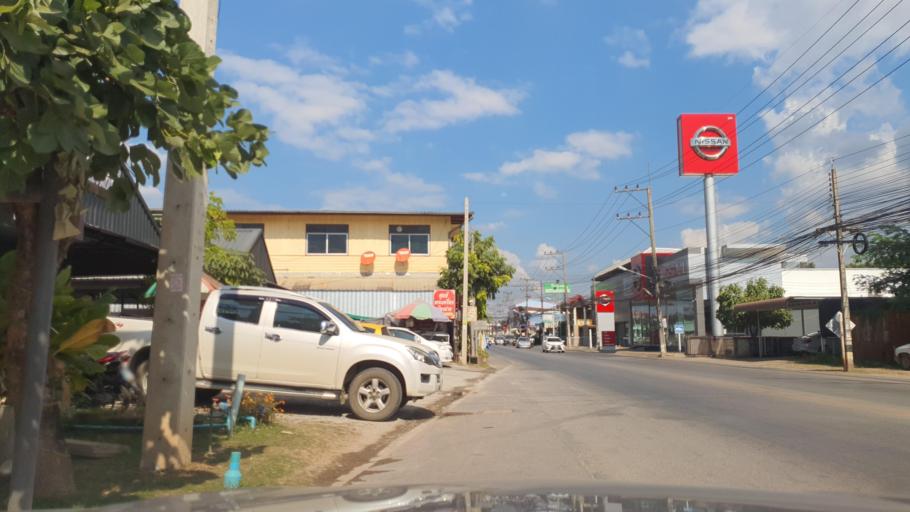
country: TH
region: Nan
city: Nan
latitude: 18.7863
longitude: 100.7753
